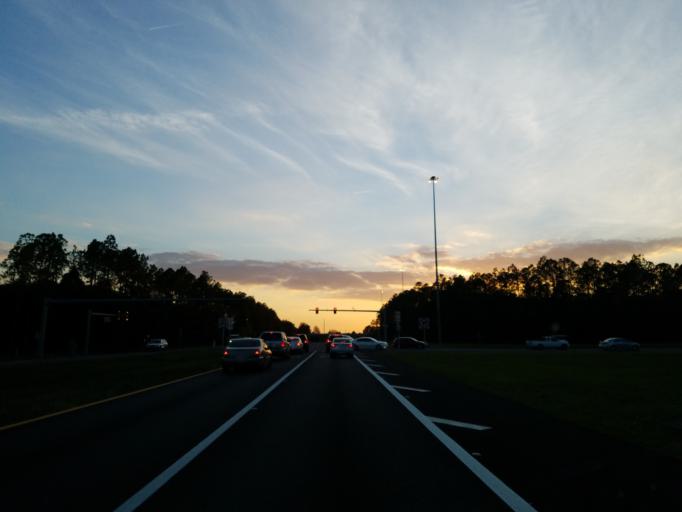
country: US
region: Florida
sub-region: Hillsborough County
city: Thonotosassa
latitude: 28.0724
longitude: -82.3485
